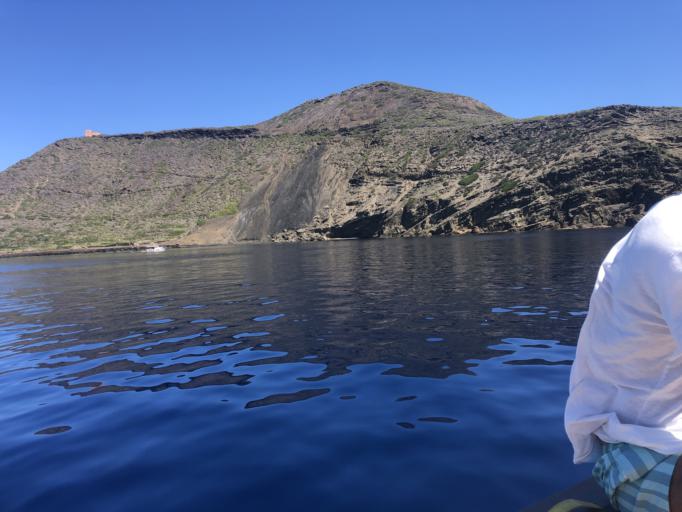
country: IT
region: Sicily
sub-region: Agrigento
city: Lampedusa
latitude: 35.8531
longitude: 12.8733
